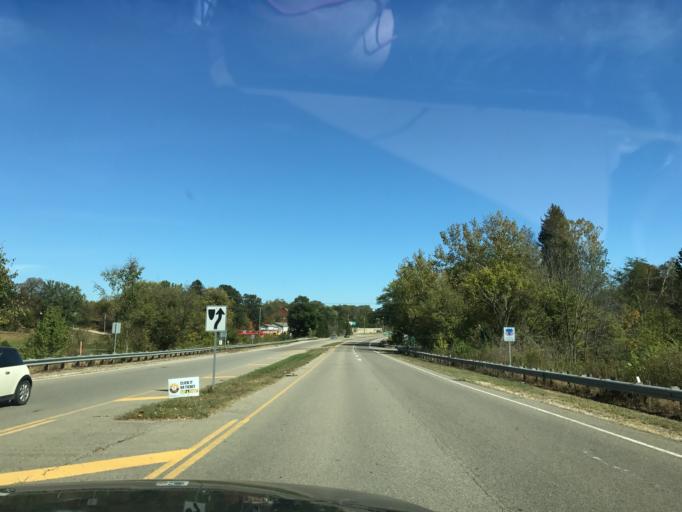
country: US
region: Ohio
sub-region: Muskingum County
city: New Concord
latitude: 39.9945
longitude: -81.7263
